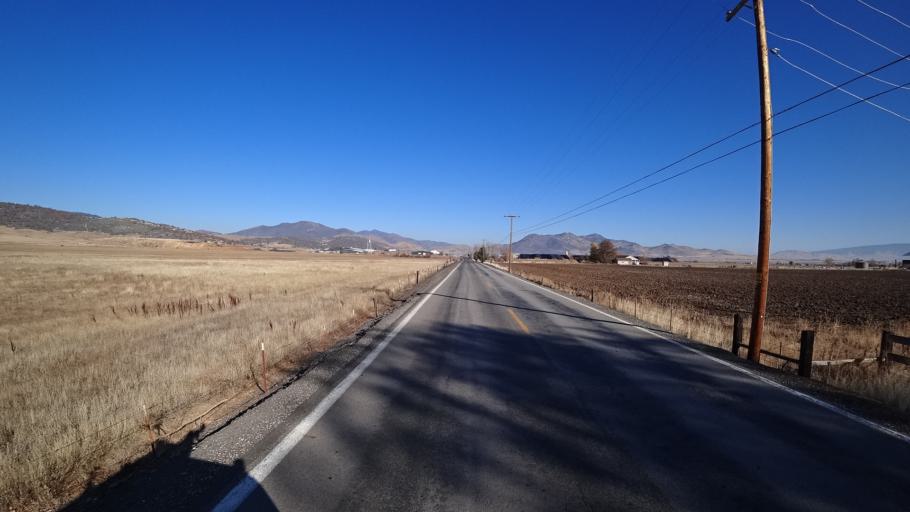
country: US
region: California
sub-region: Siskiyou County
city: Yreka
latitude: 41.7234
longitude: -122.5934
